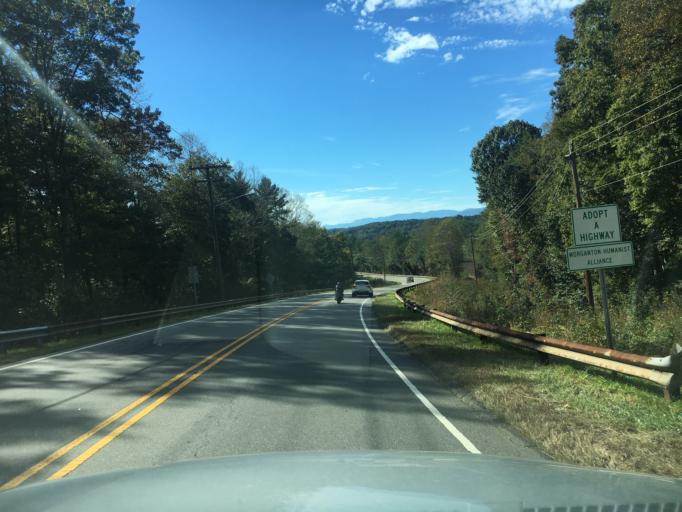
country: US
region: North Carolina
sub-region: Burke County
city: Morganton
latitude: 35.7640
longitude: -81.6923
